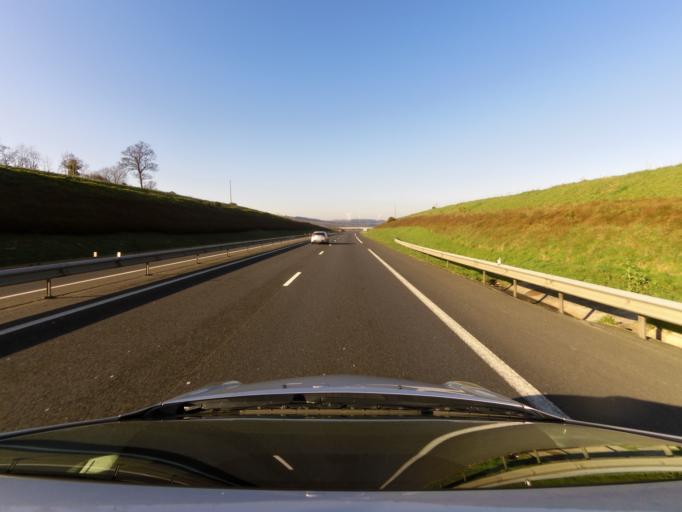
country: FR
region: Lower Normandy
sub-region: Departement de la Manche
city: Saint-Amand
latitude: 48.9940
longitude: -0.9189
